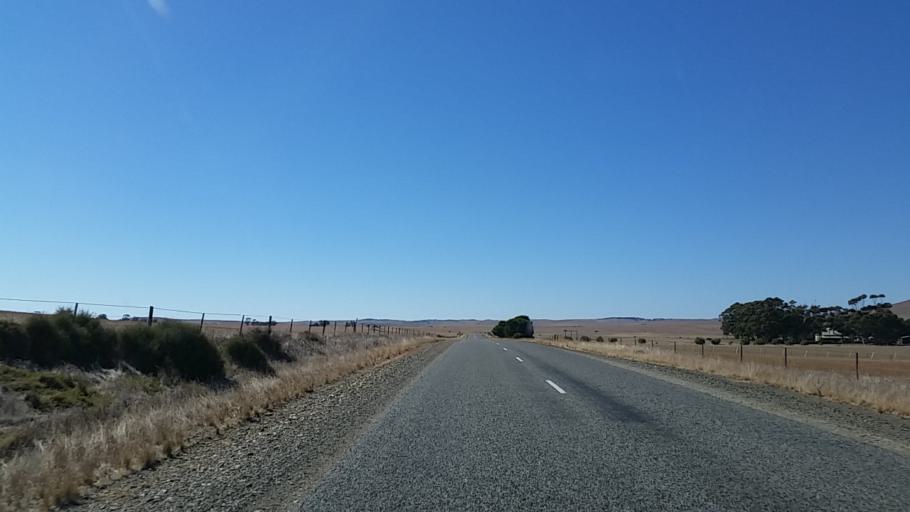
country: AU
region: South Australia
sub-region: Northern Areas
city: Jamestown
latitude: -33.3527
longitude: 138.8889
